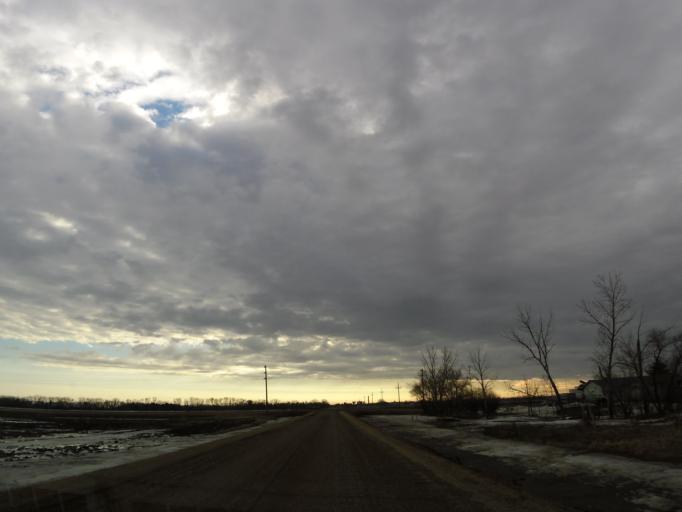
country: US
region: North Dakota
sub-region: Walsh County
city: Grafton
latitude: 48.4197
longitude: -97.4503
